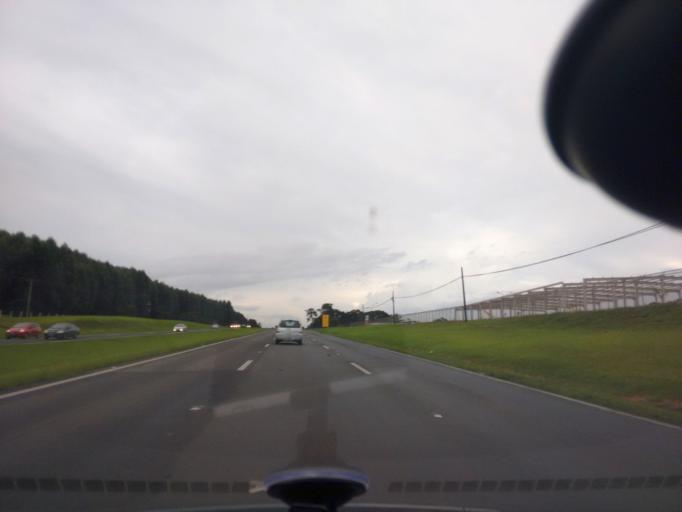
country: BR
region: Sao Paulo
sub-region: Sao Carlos
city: Sao Carlos
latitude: -22.0550
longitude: -47.8553
